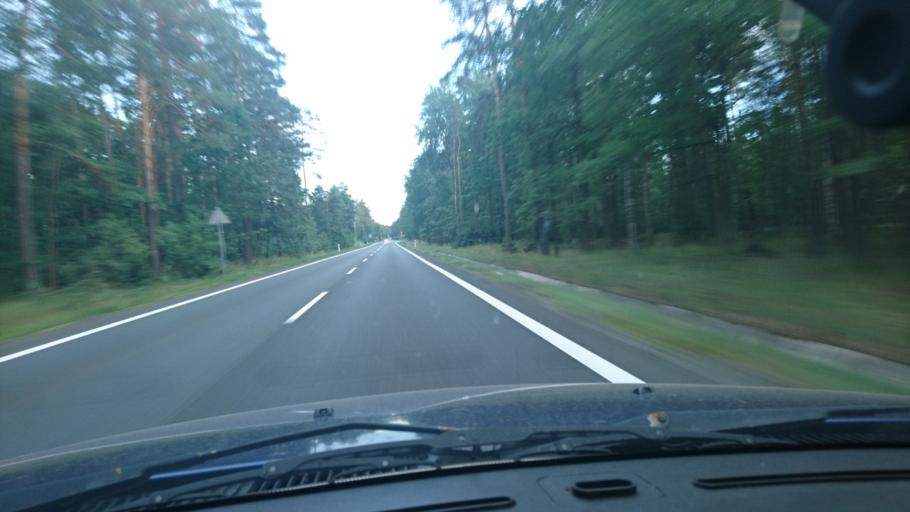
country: PL
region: Silesian Voivodeship
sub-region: Powiat lubliniecki
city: Lubliniec
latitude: 50.6089
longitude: 18.6955
